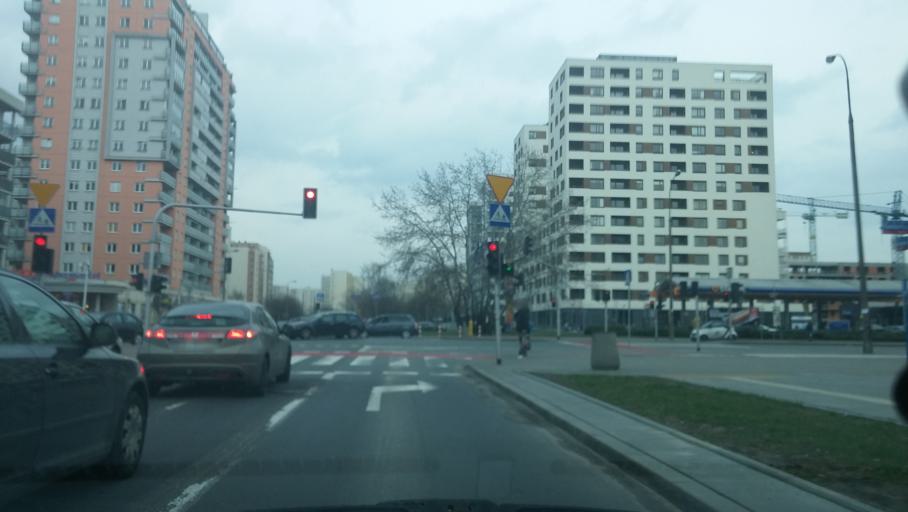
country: PL
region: Masovian Voivodeship
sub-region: Warszawa
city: Praga Poludnie
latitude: 52.2220
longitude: 21.0905
